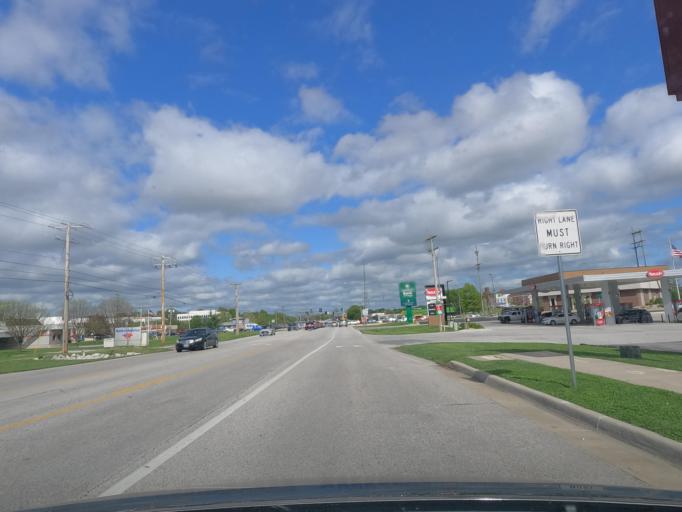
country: US
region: Missouri
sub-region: Greene County
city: Battlefield
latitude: 37.1382
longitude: -93.2981
